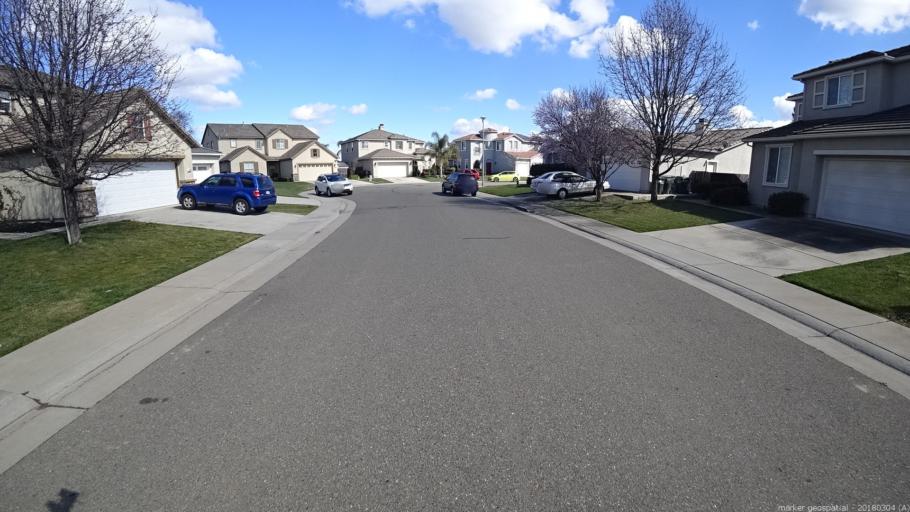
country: US
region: California
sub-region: Sacramento County
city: Vineyard
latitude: 38.4667
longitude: -121.3327
